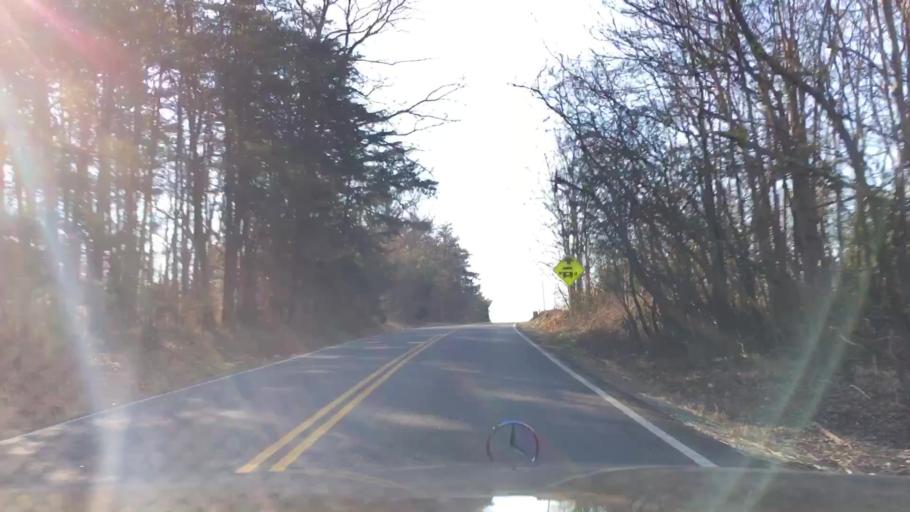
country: US
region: Virginia
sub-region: City of Bedford
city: Bedford
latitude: 37.2096
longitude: -79.4300
